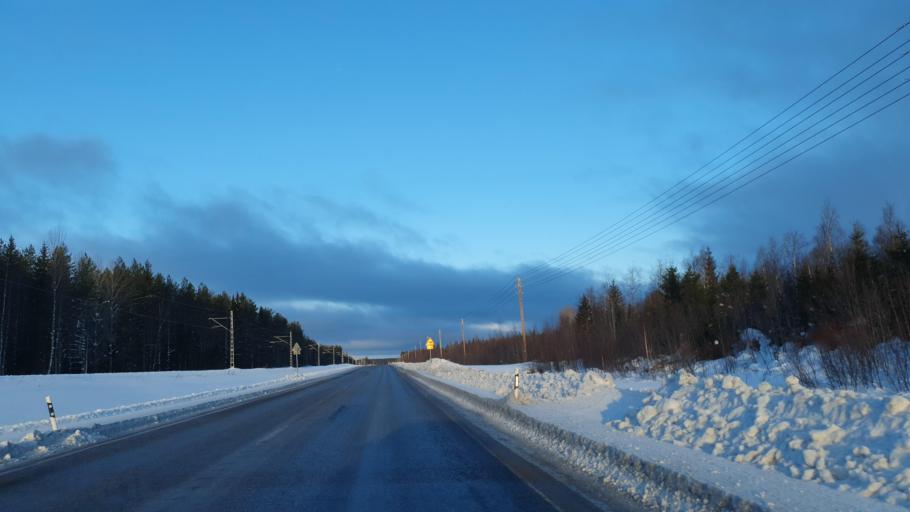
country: FI
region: Kainuu
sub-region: Kajaani
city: Paltamo
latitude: 64.4105
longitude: 27.7551
